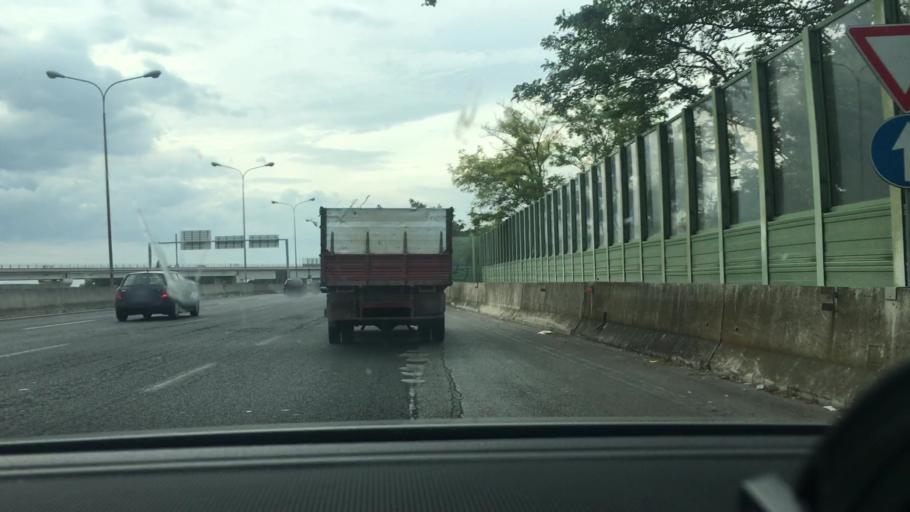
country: IT
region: Apulia
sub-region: Provincia di Bari
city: Bari
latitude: 41.0919
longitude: 16.8473
